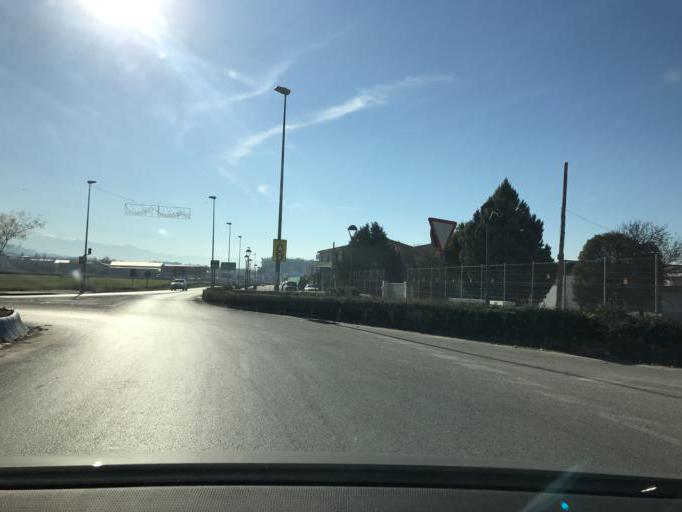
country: ES
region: Andalusia
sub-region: Provincia de Granada
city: Pulianas
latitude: 37.2178
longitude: -3.6098
